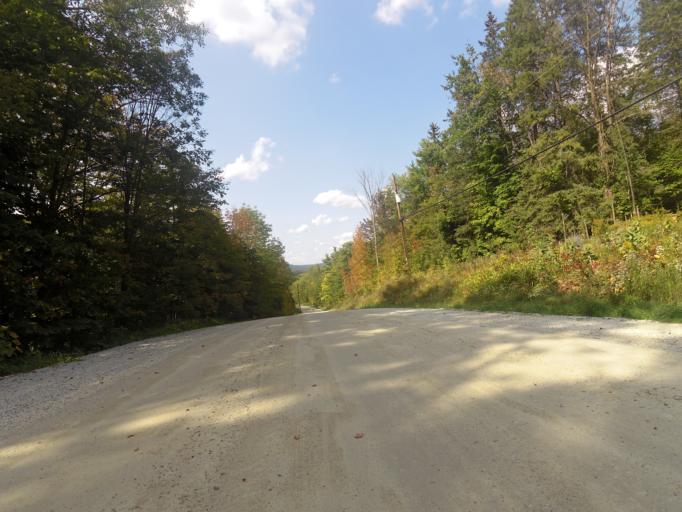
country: CA
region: Ontario
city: Renfrew
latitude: 45.1507
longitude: -76.6788
